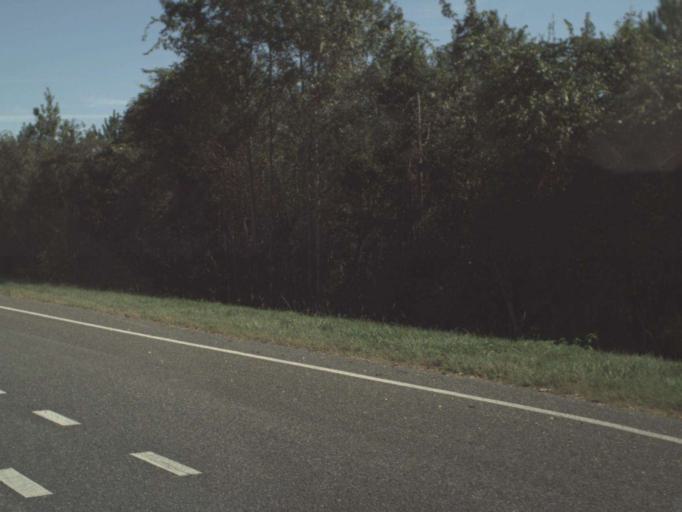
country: US
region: Florida
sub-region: Washington County
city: Chipley
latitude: 30.7468
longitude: -85.3844
